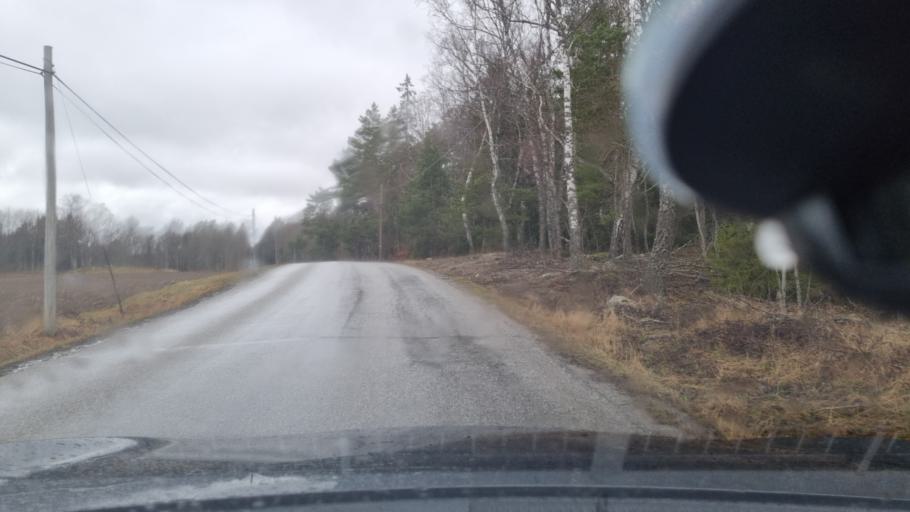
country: SE
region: Stockholm
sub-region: Sigtuna Kommun
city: Sigtuna
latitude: 59.5637
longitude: 17.7071
